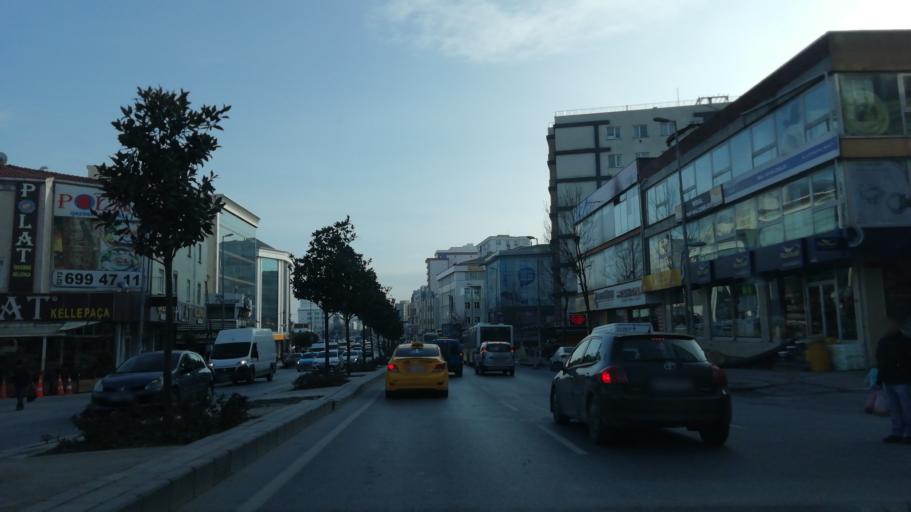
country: TR
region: Istanbul
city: Esenyurt
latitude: 41.0435
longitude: 28.6756
